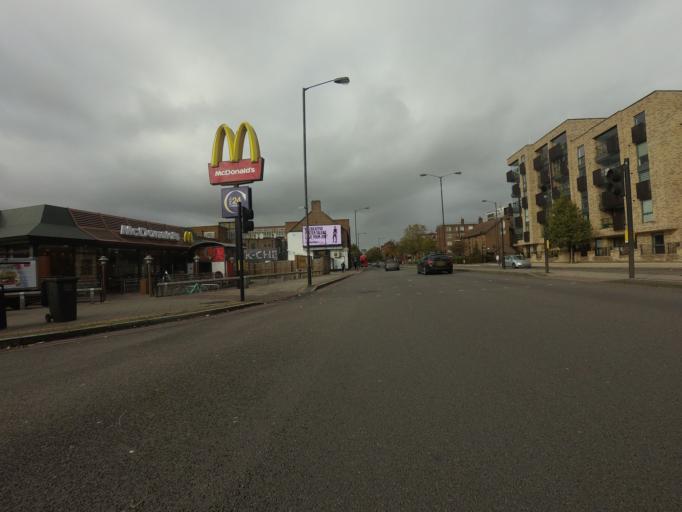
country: GB
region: England
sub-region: Greater London
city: Camberwell
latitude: 51.4846
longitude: -0.0679
